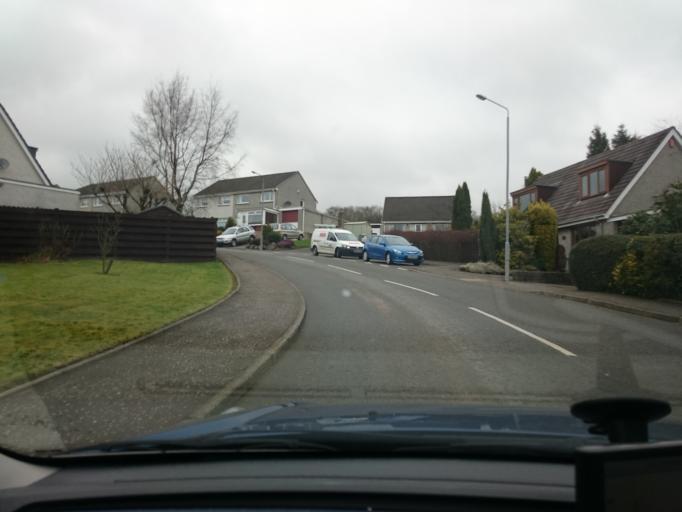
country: GB
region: Scotland
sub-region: North Lanarkshire
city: Kilsyth
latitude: 55.9828
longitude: -4.0582
